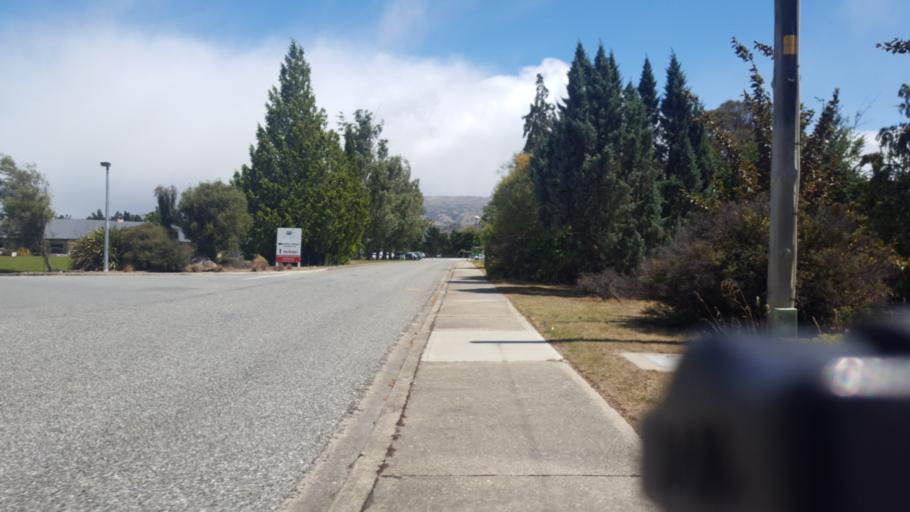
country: NZ
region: Otago
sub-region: Queenstown-Lakes District
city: Wanaka
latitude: -45.1997
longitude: 169.3311
